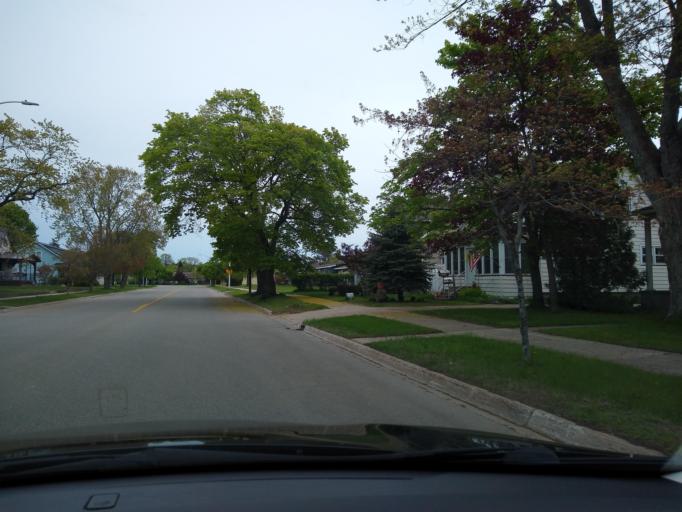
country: US
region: Michigan
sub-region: Delta County
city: Escanaba
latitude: 45.7594
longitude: -87.0698
